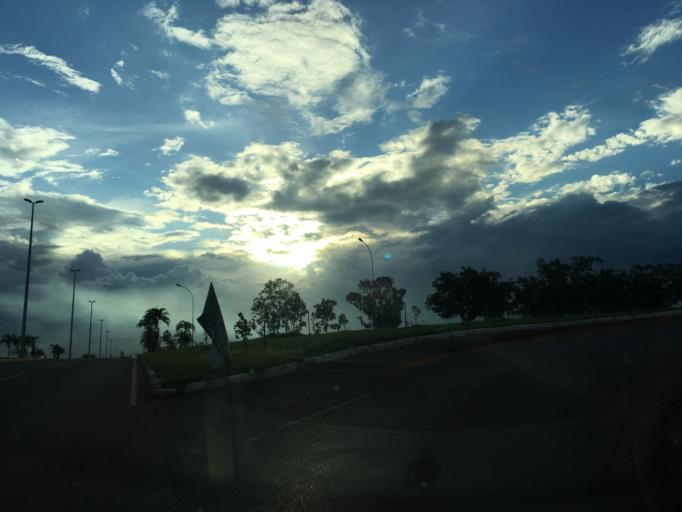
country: BR
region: Federal District
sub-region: Brasilia
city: Brasilia
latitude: -15.8119
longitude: -47.8457
